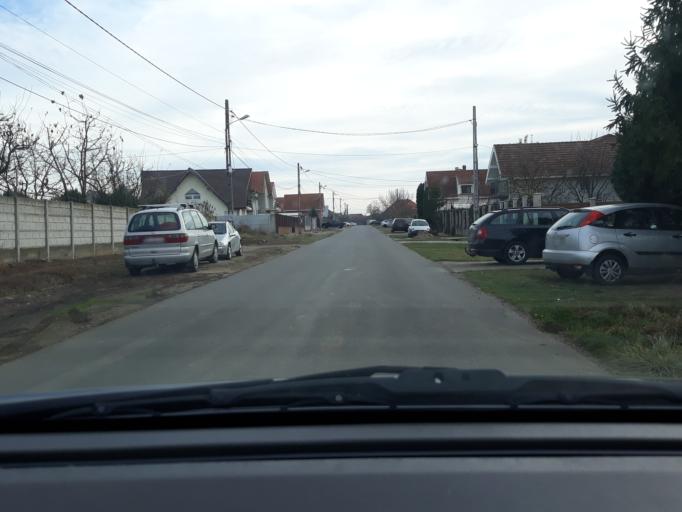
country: RO
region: Bihor
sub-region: Comuna Osorheiu
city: Alparea
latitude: 47.0177
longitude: 22.0127
